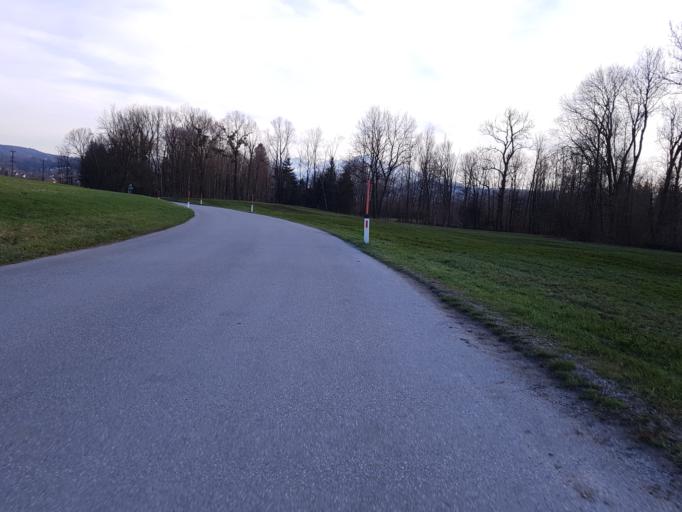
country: AT
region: Salzburg
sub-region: Politischer Bezirk Salzburg-Umgebung
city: Elsbethen
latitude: 47.7597
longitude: 13.0796
